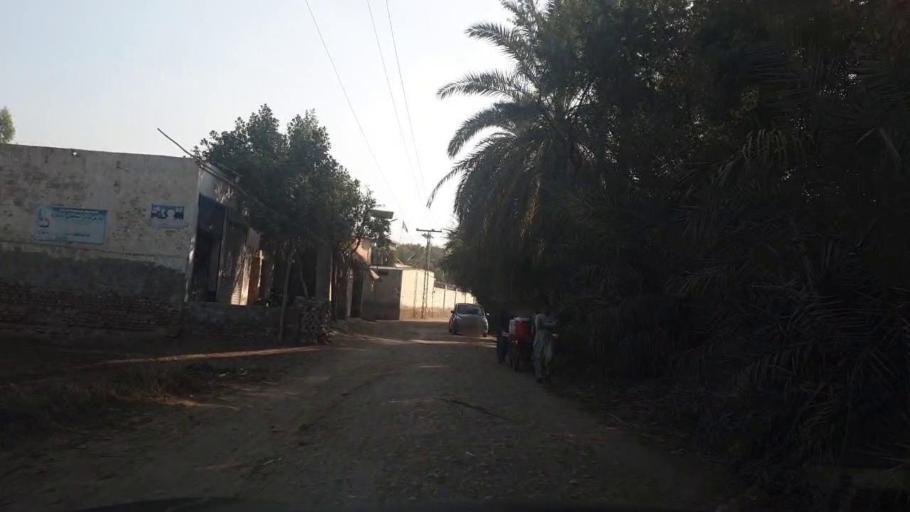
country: PK
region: Sindh
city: Ubauro
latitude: 28.1907
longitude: 69.8312
